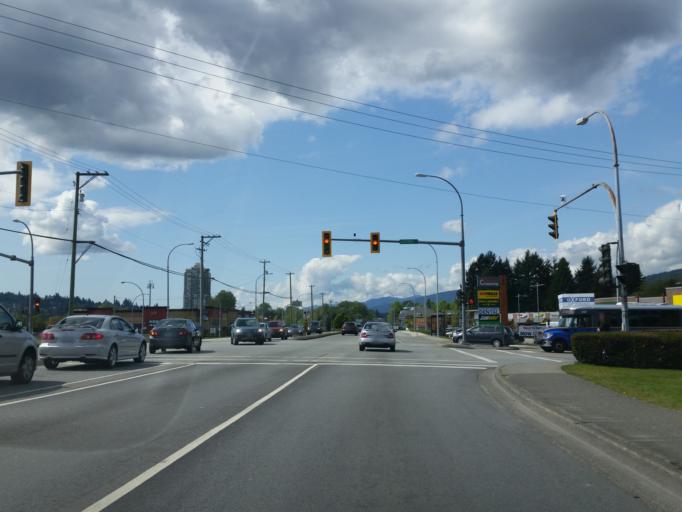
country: CA
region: British Columbia
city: Coquitlam
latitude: 49.2636
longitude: -122.7669
